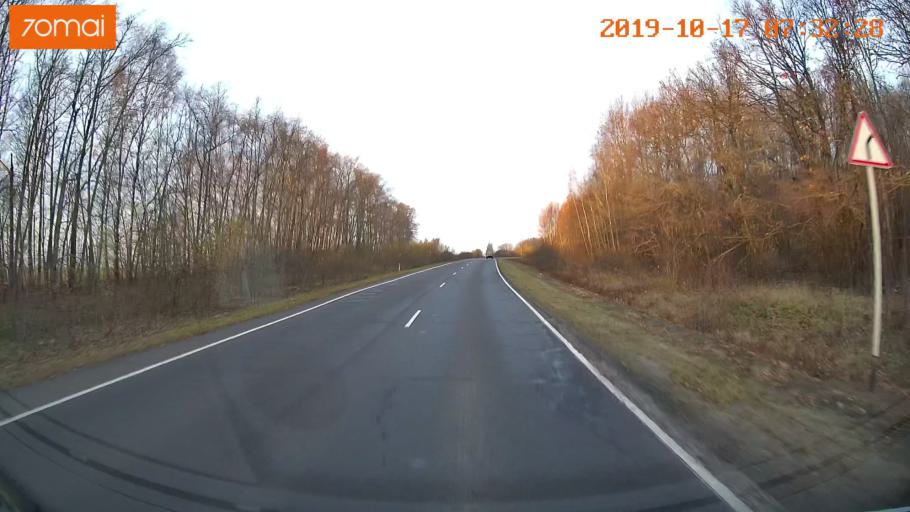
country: RU
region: Ivanovo
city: Gavrilov Posad
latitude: 56.3974
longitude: 39.9748
